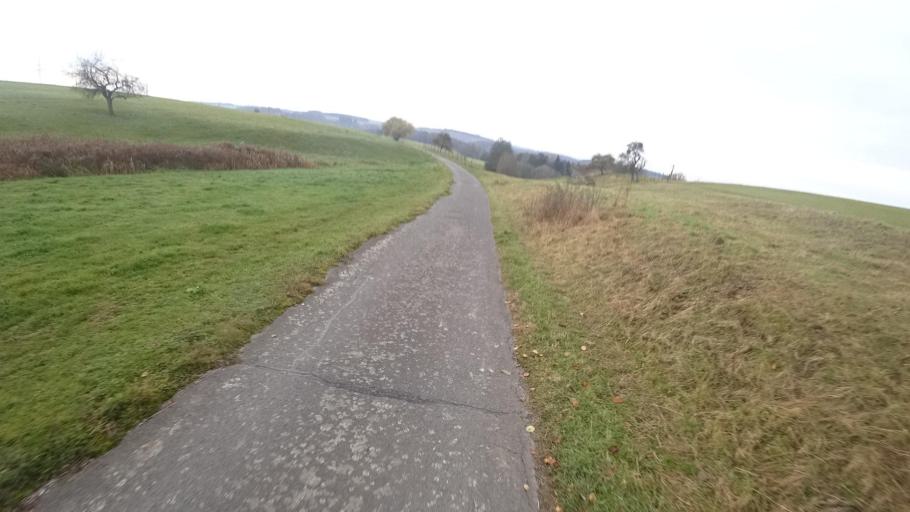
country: DE
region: Rheinland-Pfalz
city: Schwall
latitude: 50.1442
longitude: 7.5517
